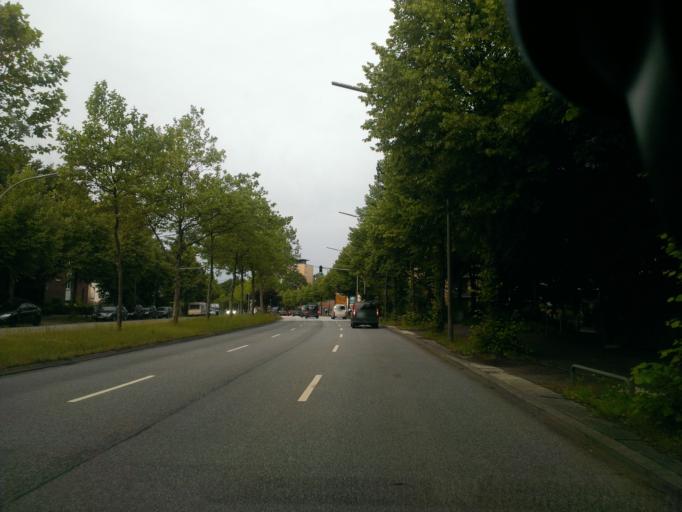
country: DE
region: Hamburg
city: Borgfelde
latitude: 53.5610
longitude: 10.0433
